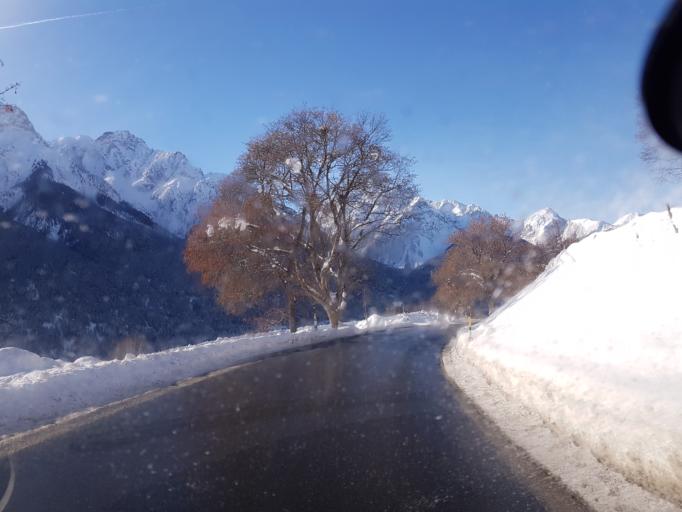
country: CH
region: Grisons
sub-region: Inn District
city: Scuol
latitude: 46.8142
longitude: 10.3297
